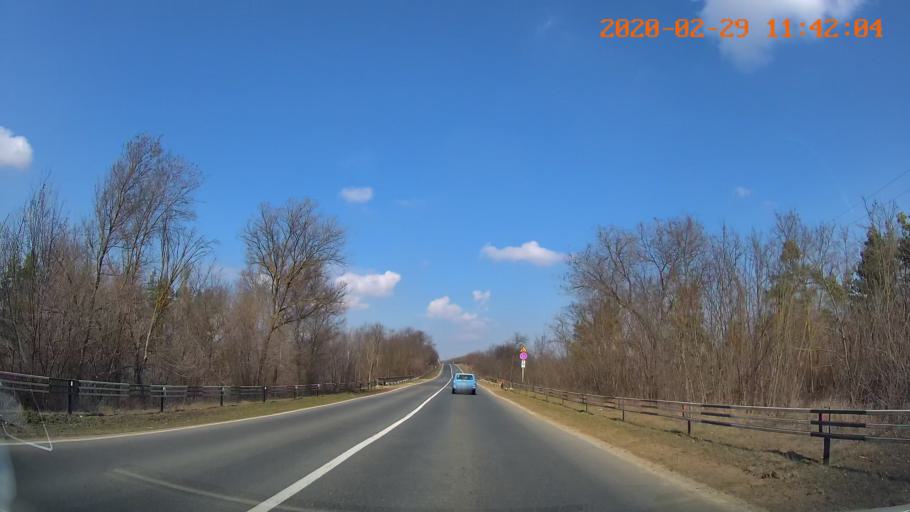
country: MD
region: Rezina
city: Saharna
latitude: 47.6794
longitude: 29.0144
